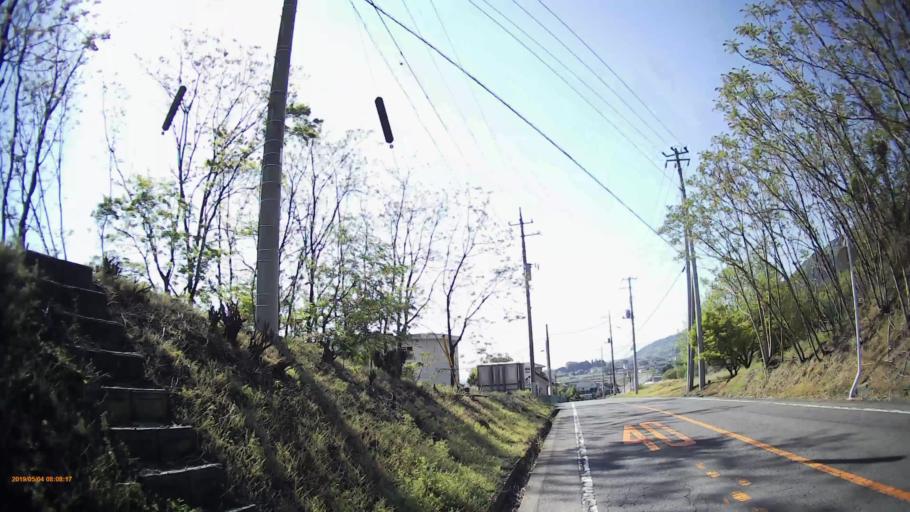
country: JP
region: Yamanashi
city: Nirasaki
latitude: 35.7402
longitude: 138.4071
